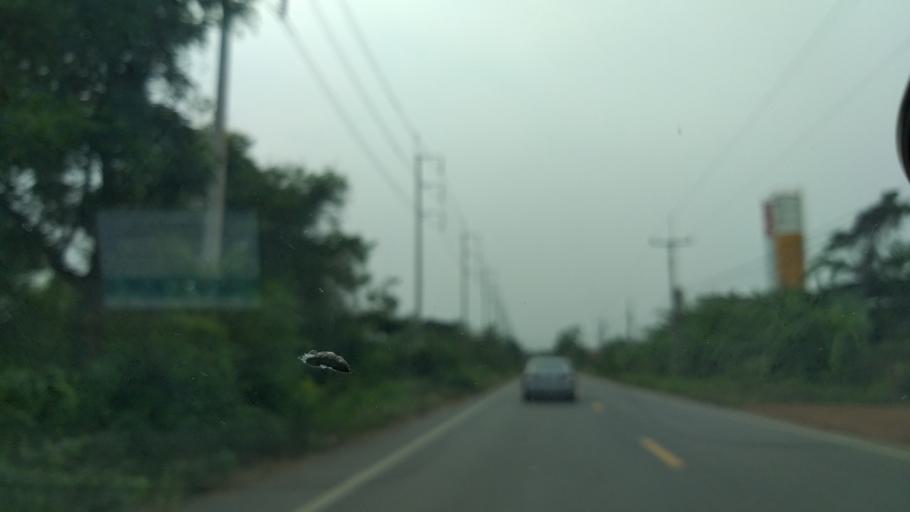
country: TH
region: Chachoengsao
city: Plaeng Yao
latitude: 13.5773
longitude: 101.2420
